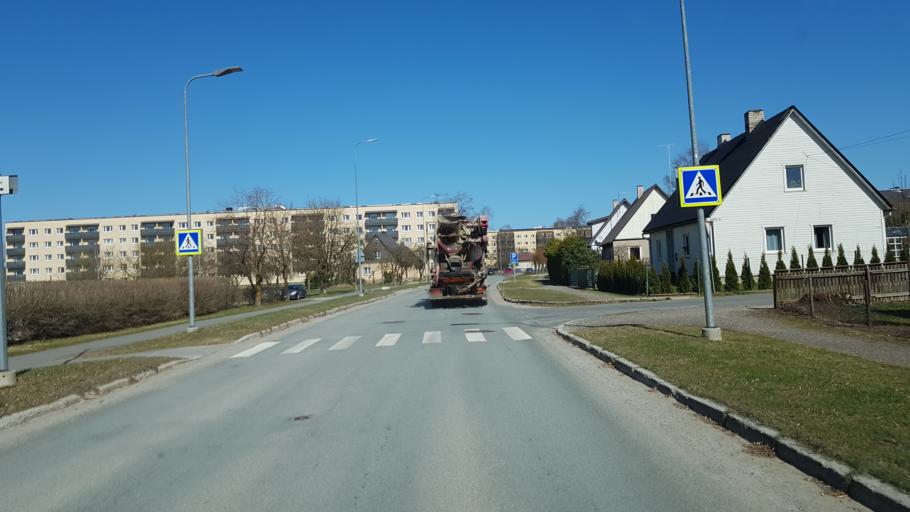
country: EE
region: Viljandimaa
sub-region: Viljandi linn
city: Viljandi
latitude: 58.3721
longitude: 25.5754
